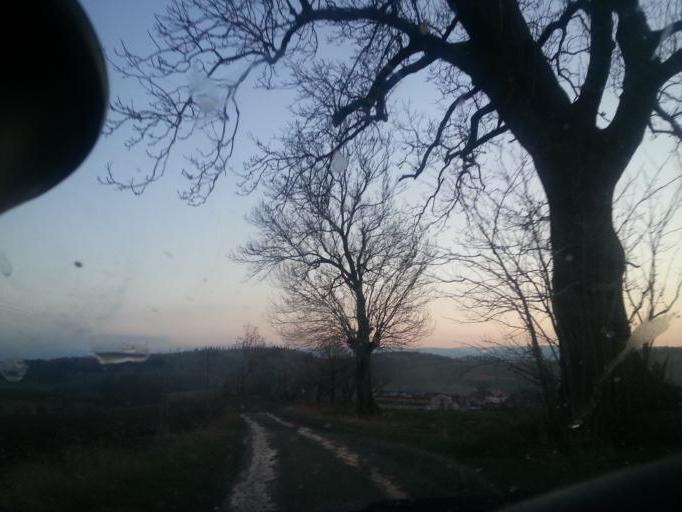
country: PL
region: Lower Silesian Voivodeship
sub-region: Powiat jeleniogorski
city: Stara Kamienica
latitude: 50.9557
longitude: 15.5852
